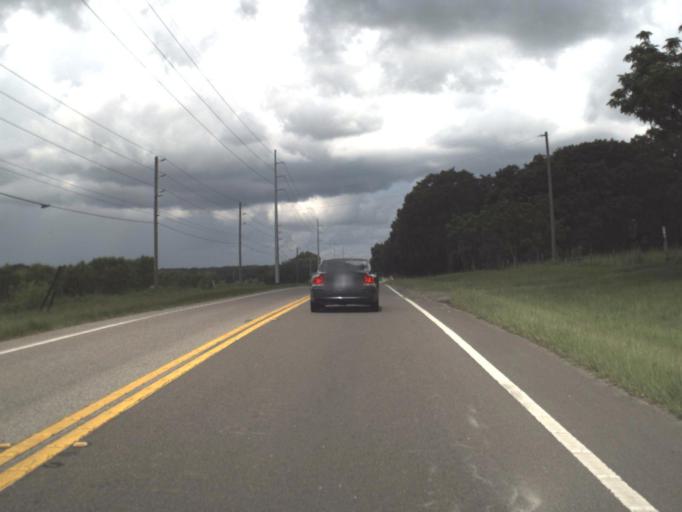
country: US
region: Florida
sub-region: Pasco County
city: San Antonio
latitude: 28.3244
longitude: -82.3497
